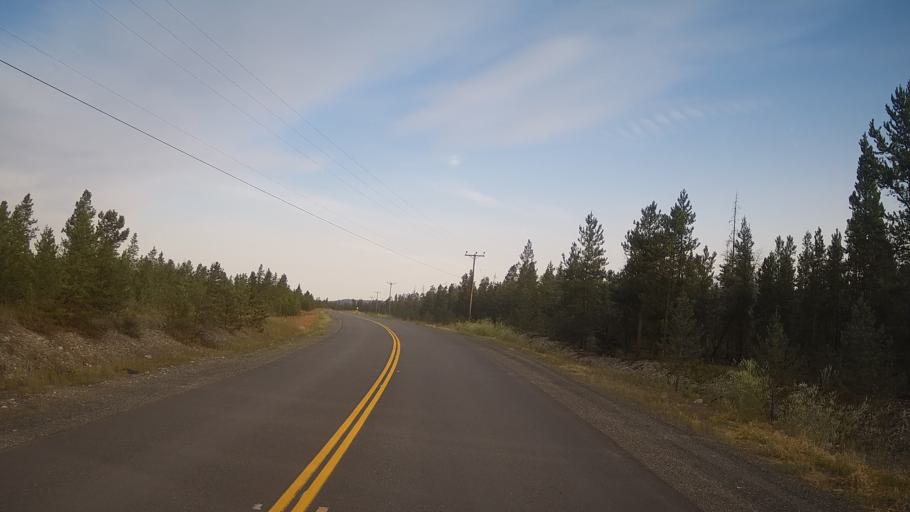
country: CA
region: British Columbia
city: Hanceville
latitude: 52.1370
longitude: -123.7035
